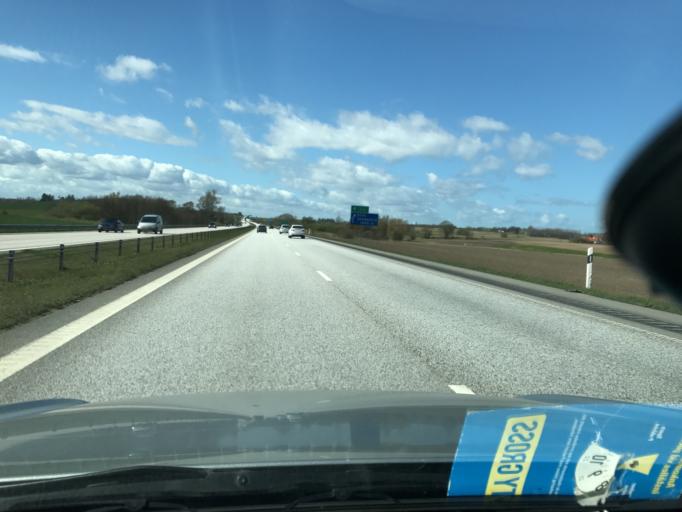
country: SE
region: Skane
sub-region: Malmo
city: Oxie
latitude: 55.5499
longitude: 13.1278
